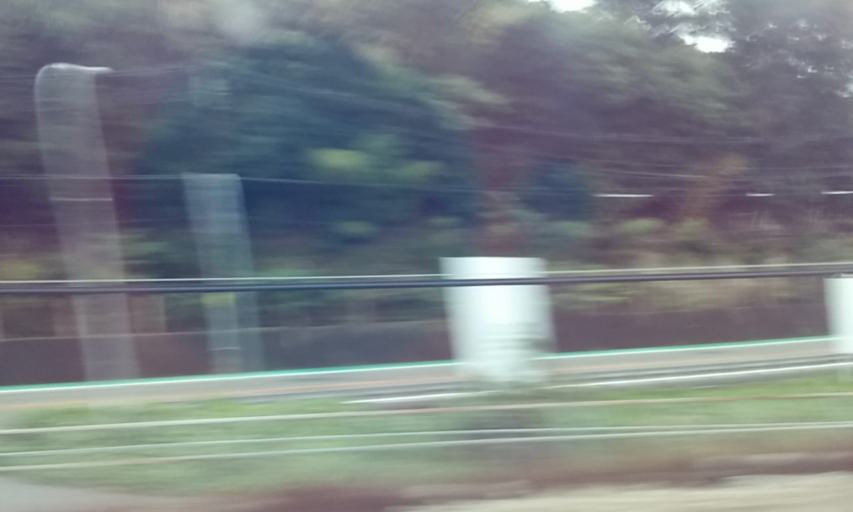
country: JP
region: Hyogo
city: Tatsunocho-tominaga
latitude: 34.8296
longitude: 134.6178
